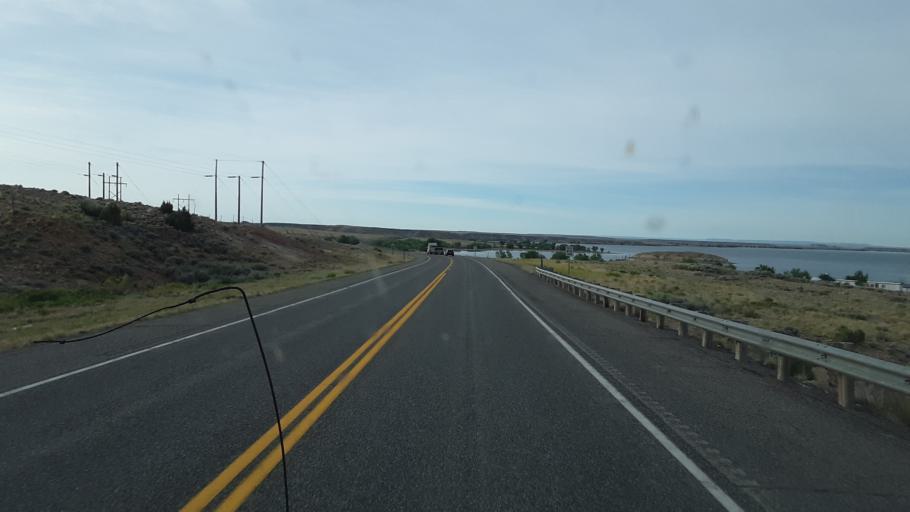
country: US
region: Wyoming
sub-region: Hot Springs County
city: Thermopolis
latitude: 43.3969
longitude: -108.1626
